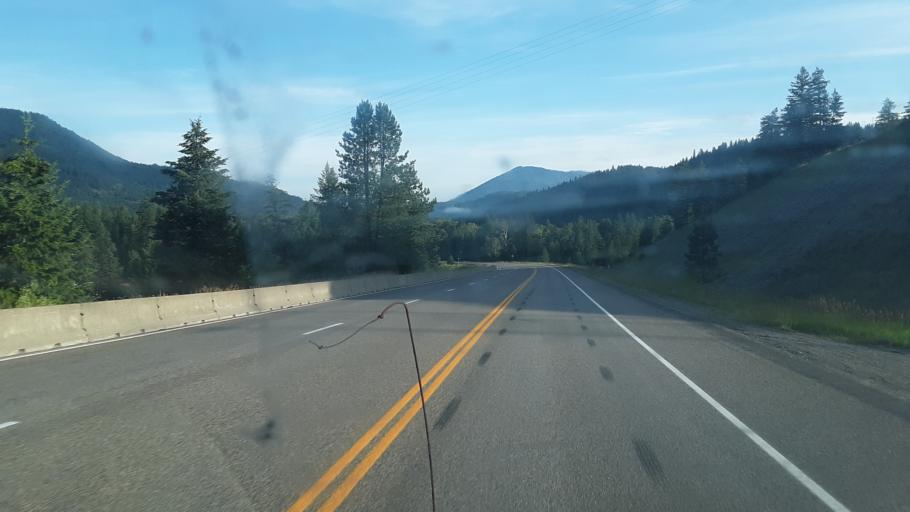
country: US
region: Montana
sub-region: Lincoln County
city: Libby
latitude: 48.4445
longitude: -115.8745
